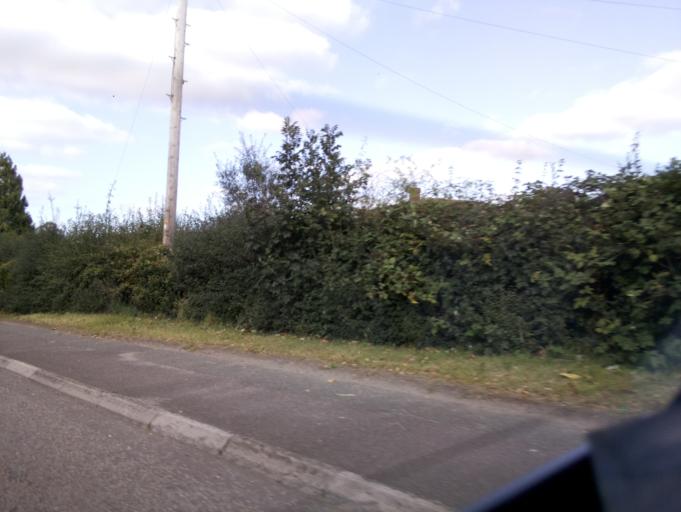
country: GB
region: England
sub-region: Hampshire
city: Basingstoke
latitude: 51.2535
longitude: -1.0790
